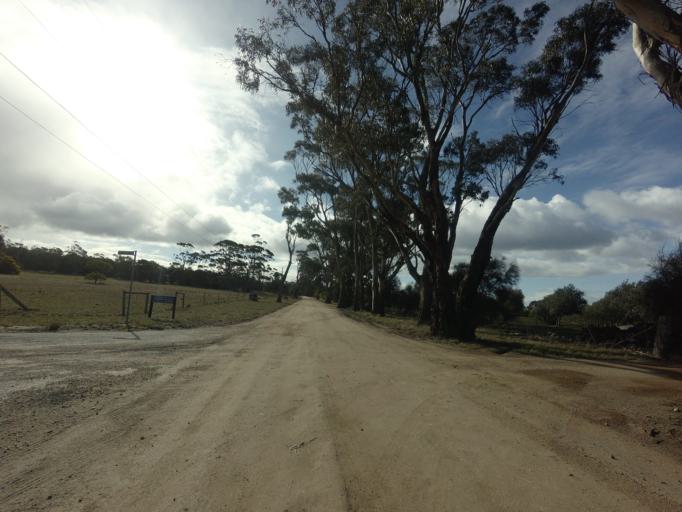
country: AU
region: Tasmania
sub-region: Sorell
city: Sorell
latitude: -42.3069
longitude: 147.9965
